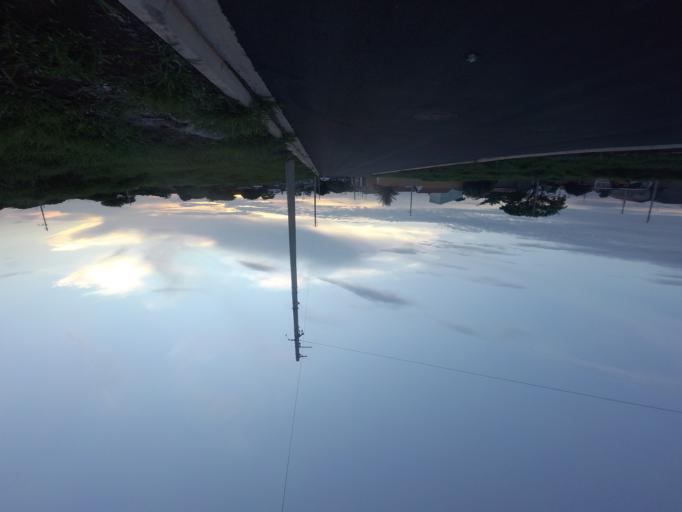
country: BR
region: Sao Paulo
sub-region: Piracicaba
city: Piracicaba
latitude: -22.7650
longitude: -47.5872
